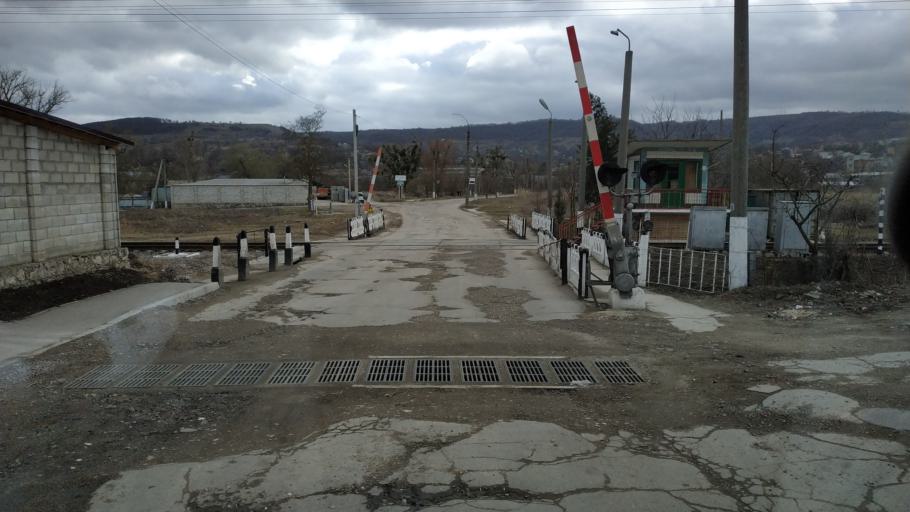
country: MD
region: Calarasi
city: Calarasi
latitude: 47.2472
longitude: 28.3169
